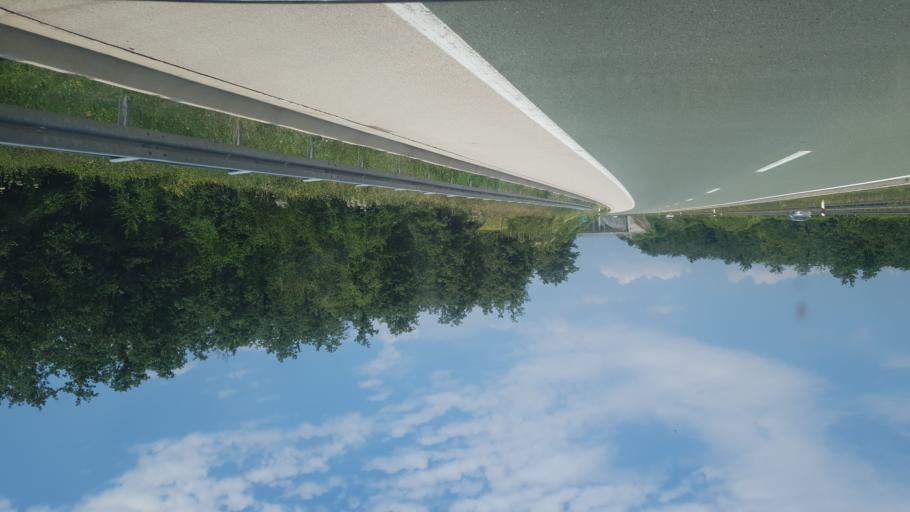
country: HR
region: Primorsko-Goranska
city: Matulji
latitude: 45.4373
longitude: 14.2783
